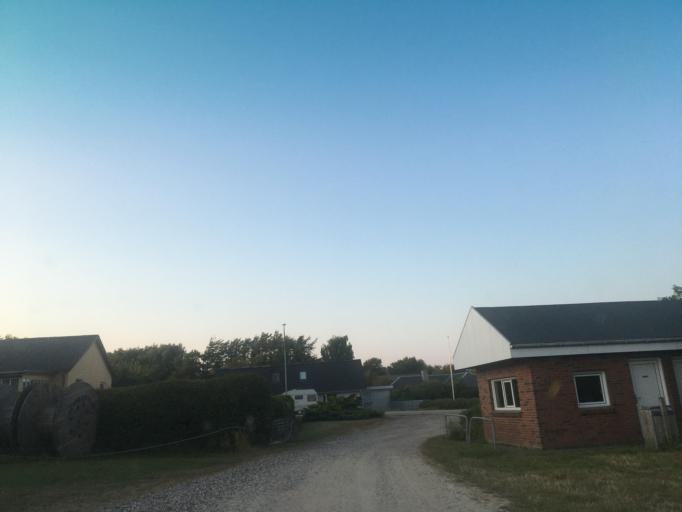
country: DK
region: North Denmark
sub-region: Thisted Kommune
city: Hurup
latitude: 56.7539
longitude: 8.4053
